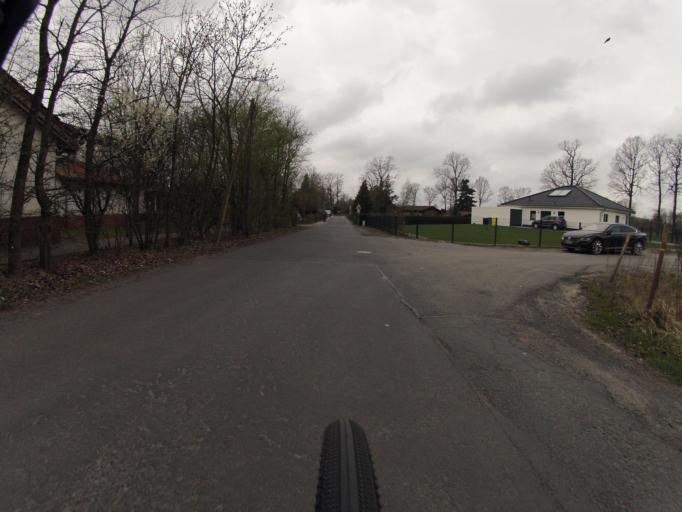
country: DE
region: North Rhine-Westphalia
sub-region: Regierungsbezirk Munster
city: Mettingen
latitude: 52.3252
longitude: 7.7723
